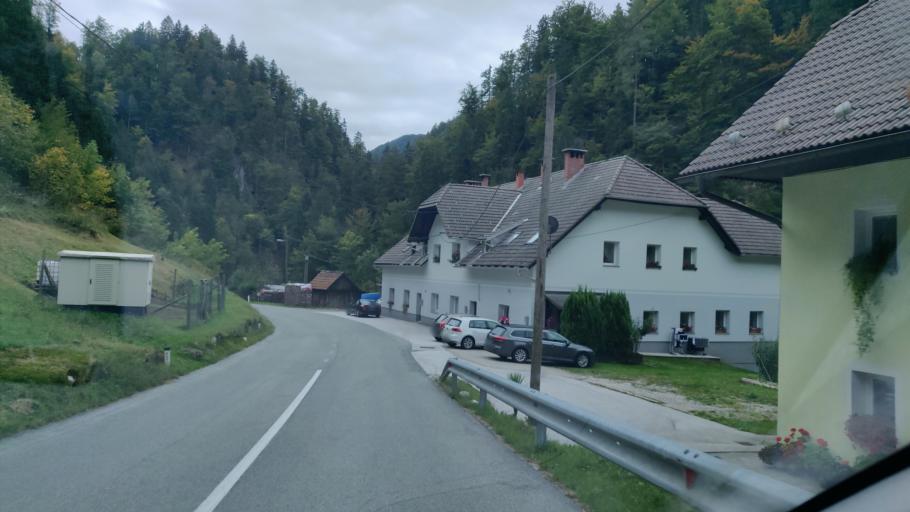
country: SI
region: Jezersko
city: Zgornje Jezersko
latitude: 46.3711
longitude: 14.4674
